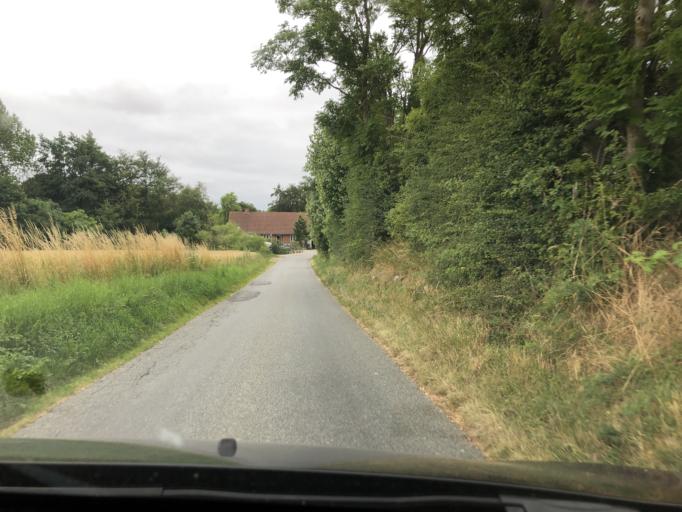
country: DK
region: South Denmark
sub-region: AEro Kommune
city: AEroskobing
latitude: 54.9139
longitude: 10.2877
